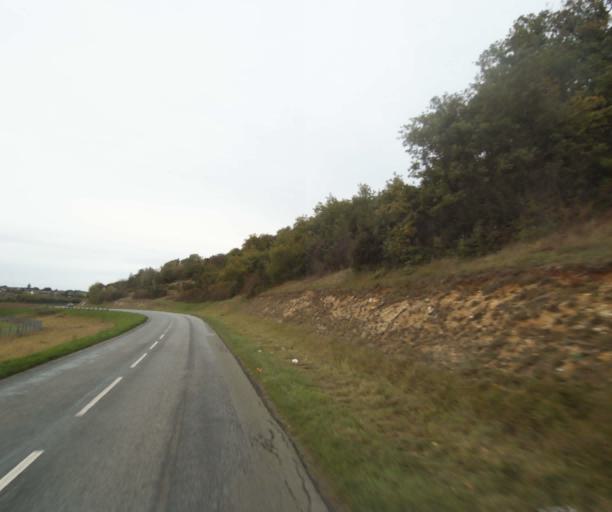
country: FR
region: Centre
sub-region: Departement d'Eure-et-Loir
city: Vert-en-Drouais
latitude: 48.7498
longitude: 1.3147
